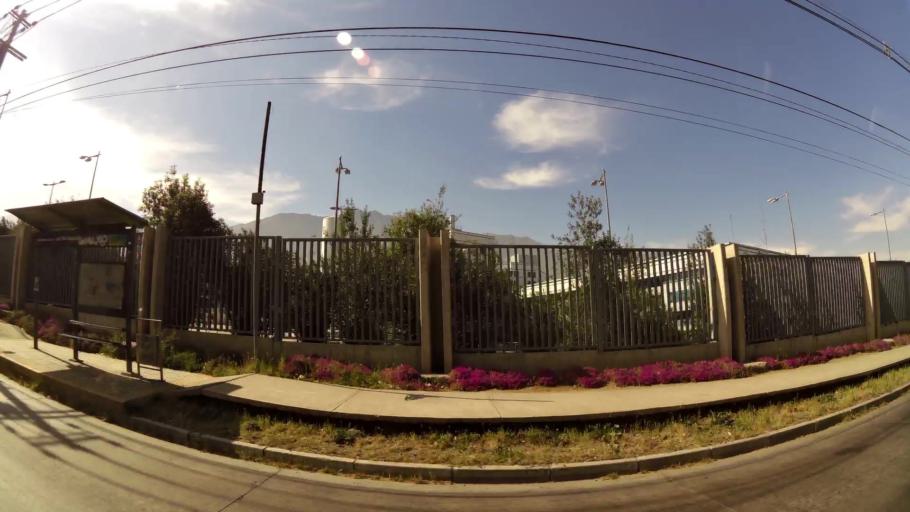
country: CL
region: Santiago Metropolitan
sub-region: Provincia de Santiago
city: Villa Presidente Frei, Nunoa, Santiago, Chile
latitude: -33.4491
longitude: -70.5394
